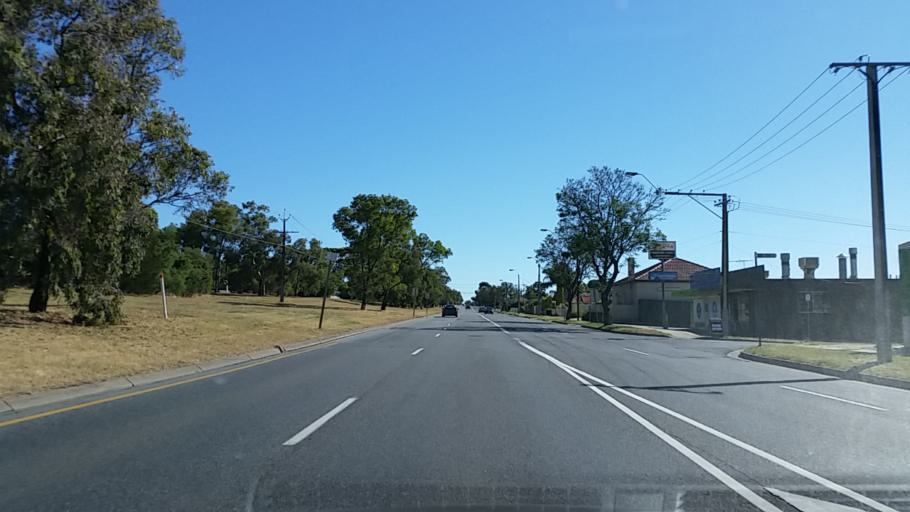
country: AU
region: South Australia
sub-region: Salisbury
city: Ingle Farm
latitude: -34.8285
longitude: 138.6319
